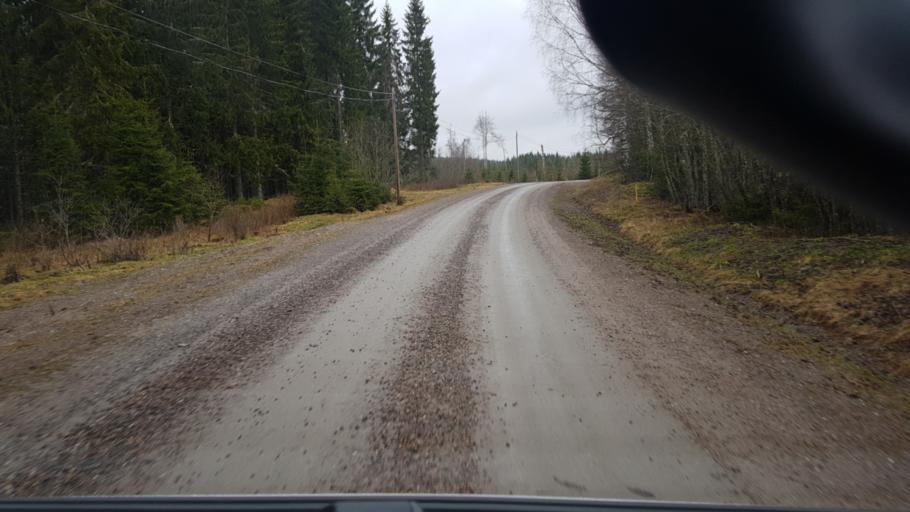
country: SE
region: Vaermland
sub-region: Eda Kommun
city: Charlottenberg
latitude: 59.9720
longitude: 12.4978
